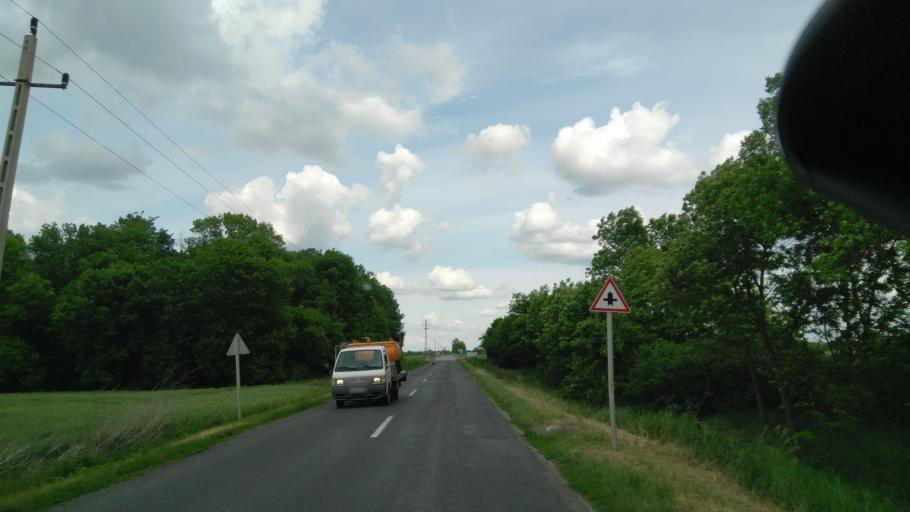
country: HU
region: Bekes
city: Battonya
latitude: 46.2933
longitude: 20.9836
